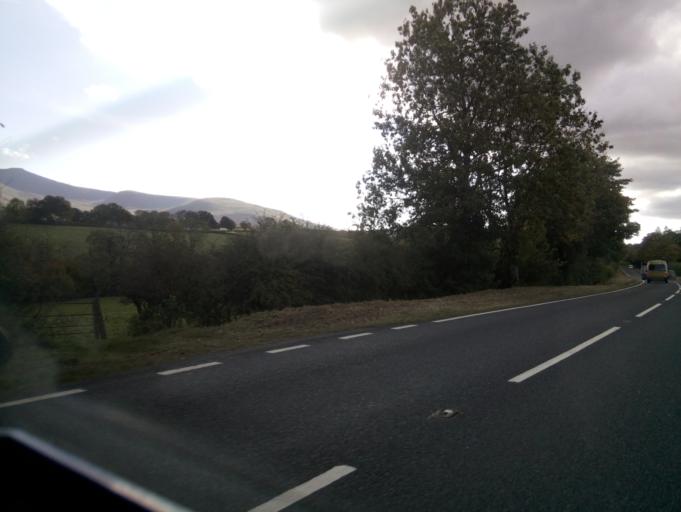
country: GB
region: Wales
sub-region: Sir Powys
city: Brecon
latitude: 51.9327
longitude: -3.4454
